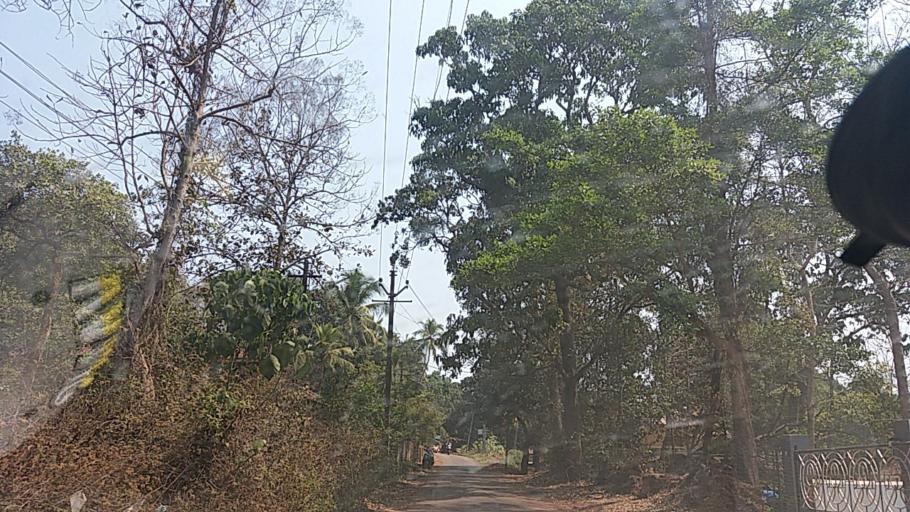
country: IN
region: Goa
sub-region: South Goa
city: Sancoale
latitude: 15.3664
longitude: 73.9149
